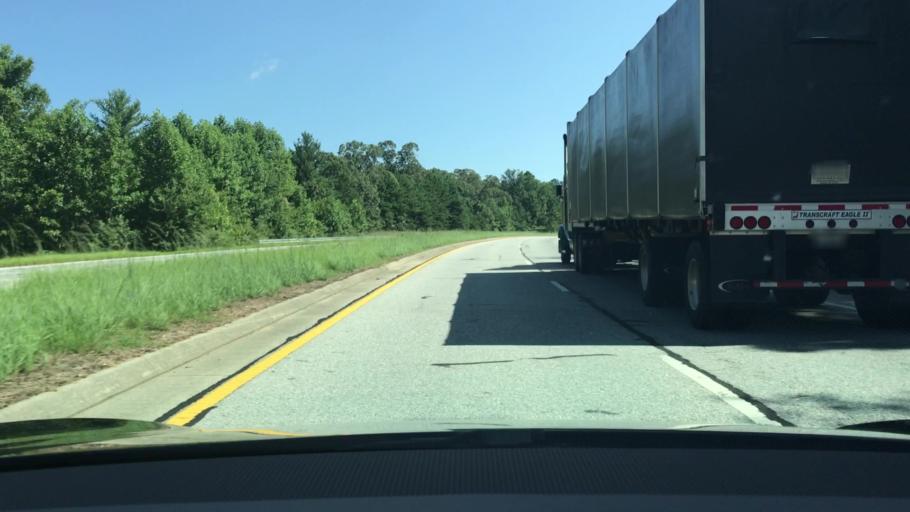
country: US
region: Georgia
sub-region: Stephens County
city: Toccoa
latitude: 34.7172
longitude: -83.3998
